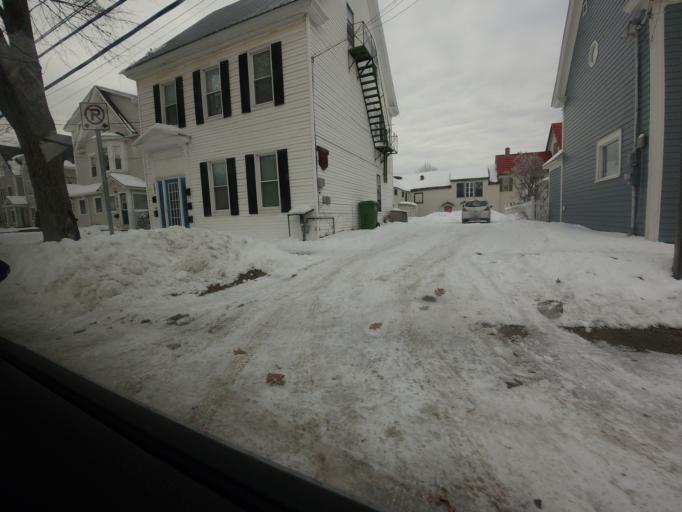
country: CA
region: New Brunswick
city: Fredericton
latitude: 45.9566
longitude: -66.6400
